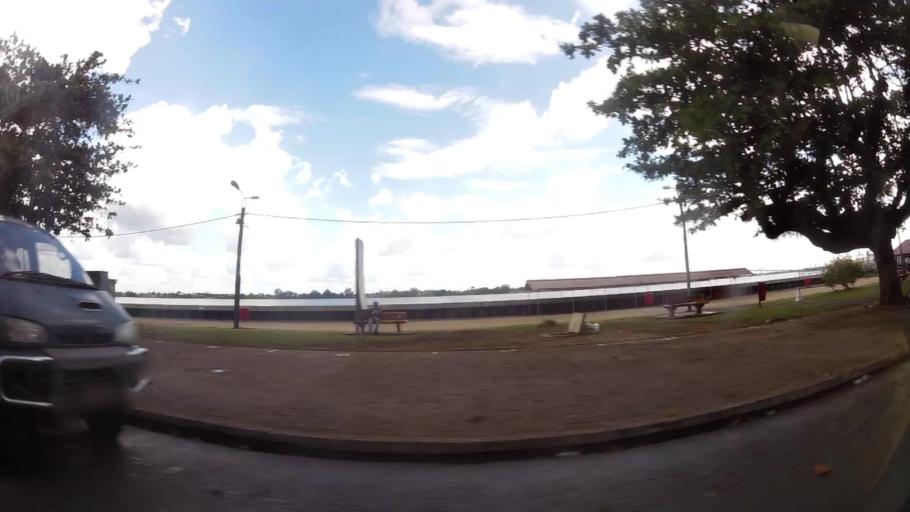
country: SR
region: Paramaribo
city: Paramaribo
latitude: 5.8252
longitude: -55.1522
